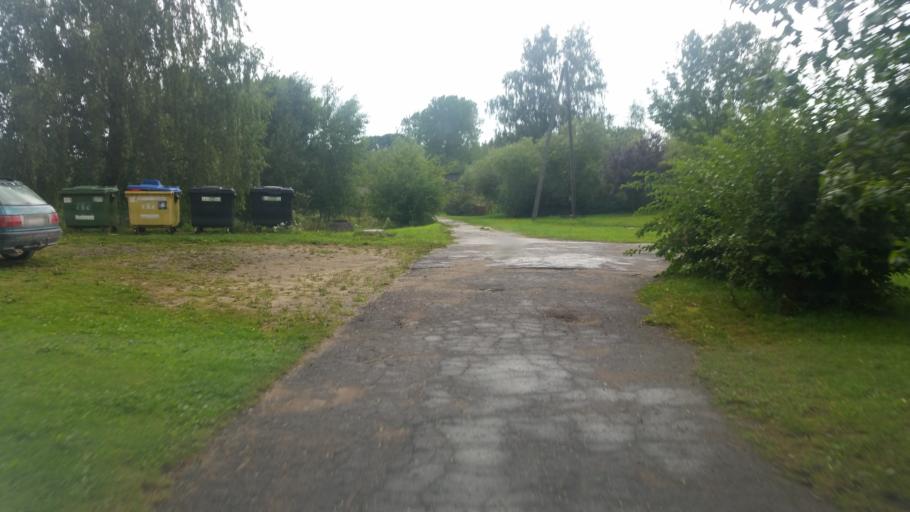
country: LV
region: Vecumnieki
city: Vecumnieki
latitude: 56.4333
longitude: 24.4615
